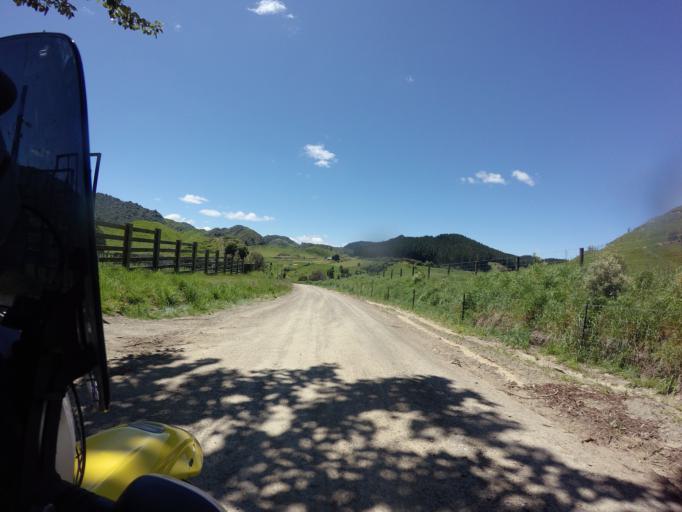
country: NZ
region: Bay of Plenty
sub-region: Opotiki District
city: Opotiki
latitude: -38.3975
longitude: 177.4587
